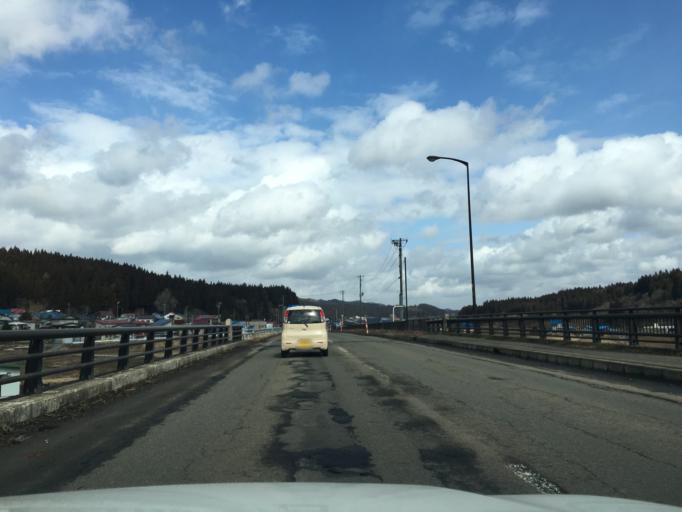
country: JP
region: Akita
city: Takanosu
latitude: 40.0299
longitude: 140.2742
